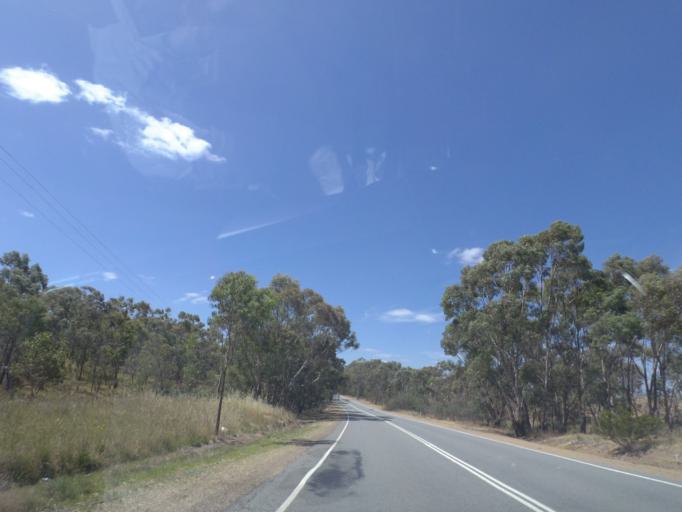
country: AU
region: Victoria
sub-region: Wangaratta
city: Wangaratta
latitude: -36.4600
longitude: 146.2341
